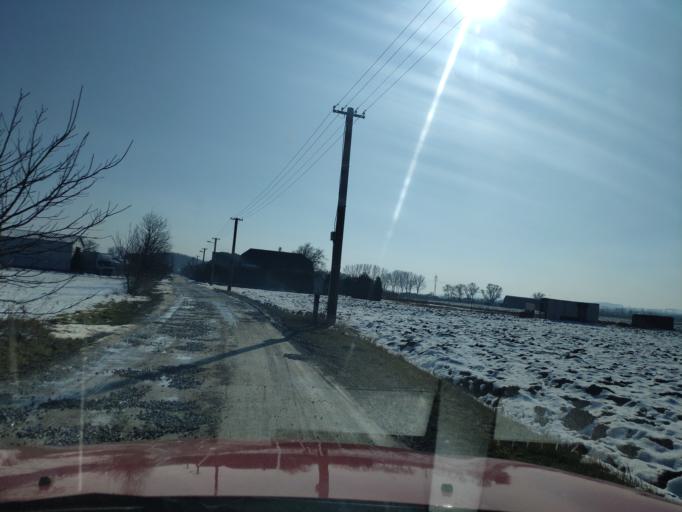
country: HU
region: Borsod-Abauj-Zemplen
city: Gonc
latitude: 48.5832
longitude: 21.2675
